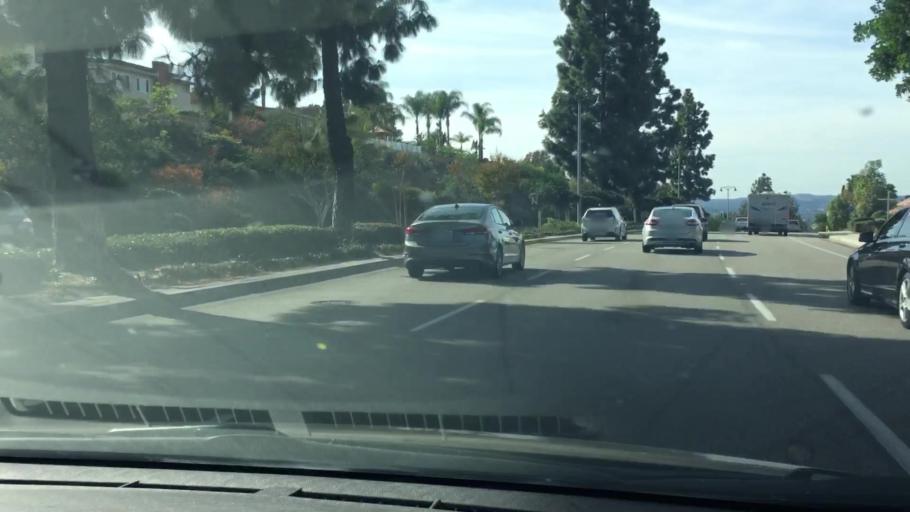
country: US
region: California
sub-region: Orange County
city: Mission Viejo
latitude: 33.6210
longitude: -117.6652
